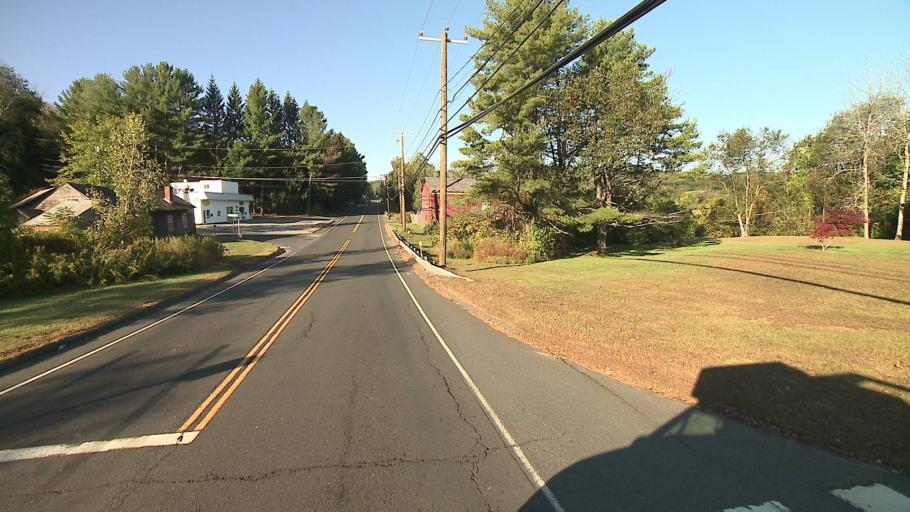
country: US
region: Connecticut
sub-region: Litchfield County
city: Northwest Harwinton
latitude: 41.8305
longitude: -73.0328
